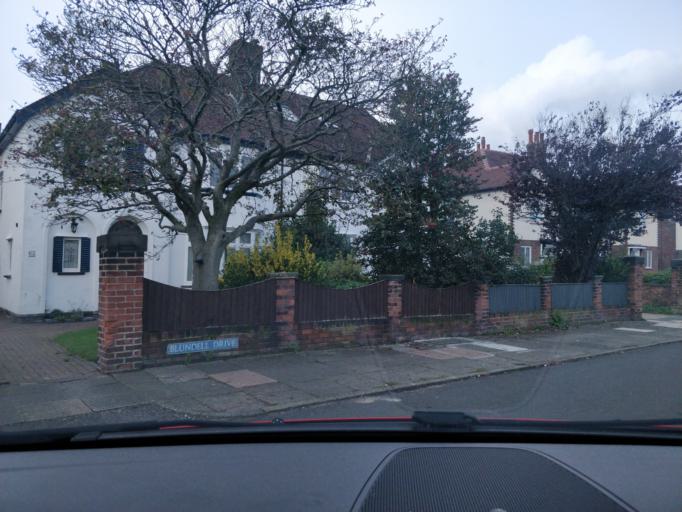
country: GB
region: England
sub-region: Sefton
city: Southport
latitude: 53.6237
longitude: -3.0203
